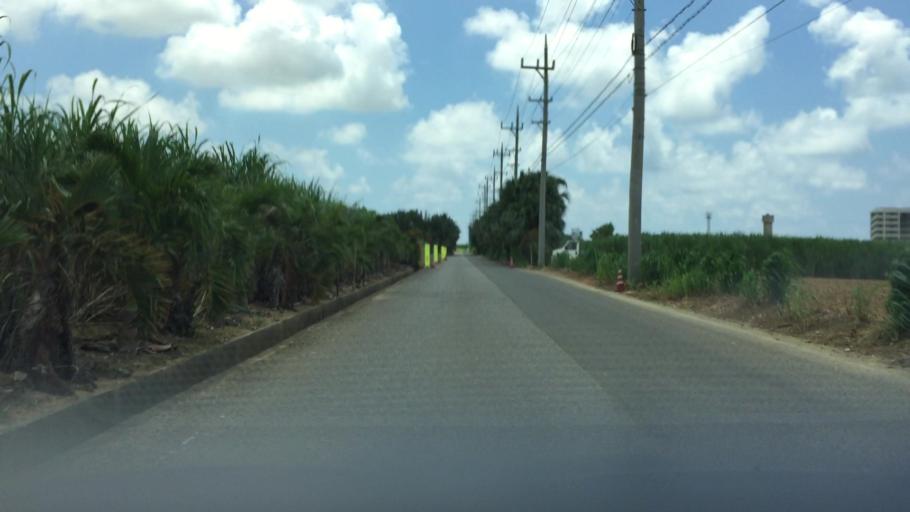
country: JP
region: Okinawa
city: Ishigaki
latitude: 24.3595
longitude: 124.1406
